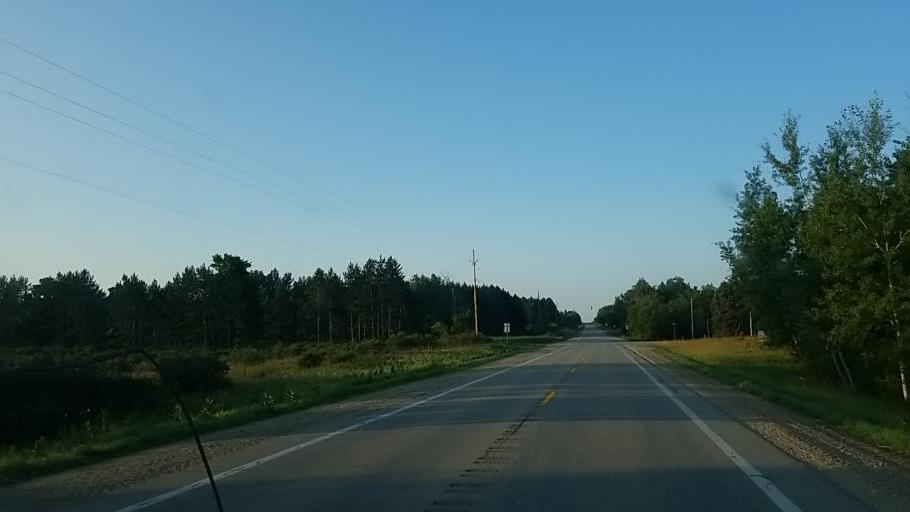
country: US
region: Michigan
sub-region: Isabella County
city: Lake Isabella
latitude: 43.6265
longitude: -85.1461
